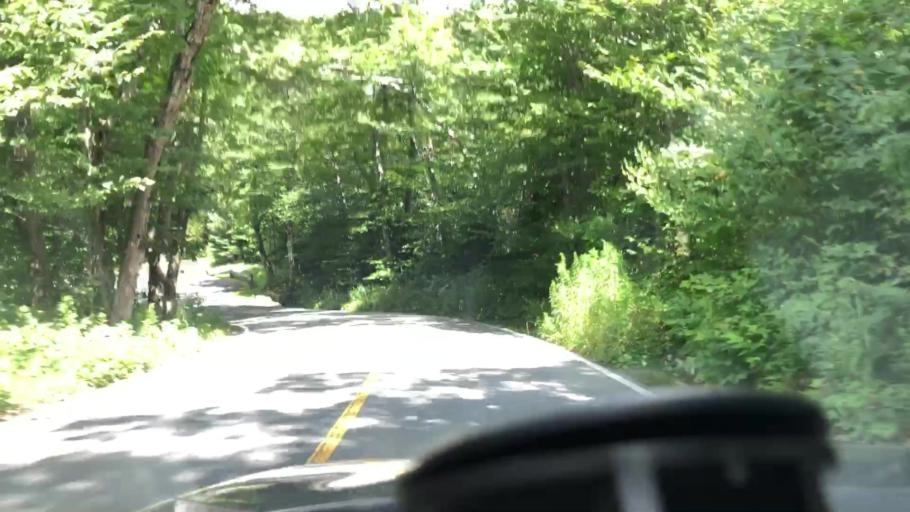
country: US
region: Massachusetts
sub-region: Berkshire County
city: Adams
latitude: 42.6625
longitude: -73.1610
